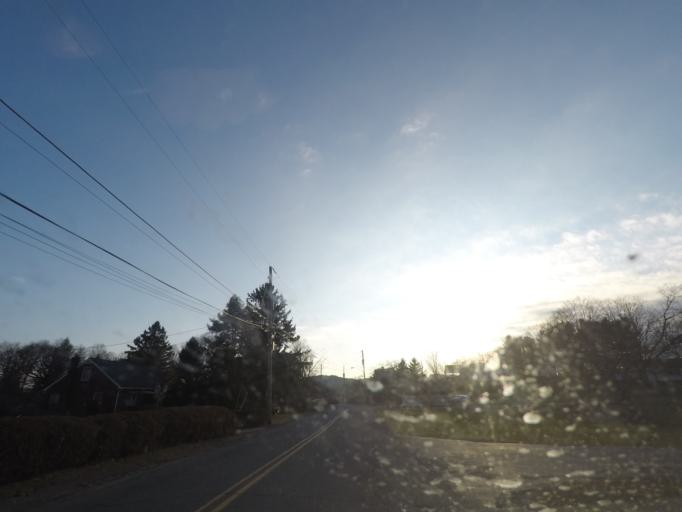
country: US
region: New York
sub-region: Rensselaer County
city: Wynantskill
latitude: 42.6956
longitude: -73.6326
